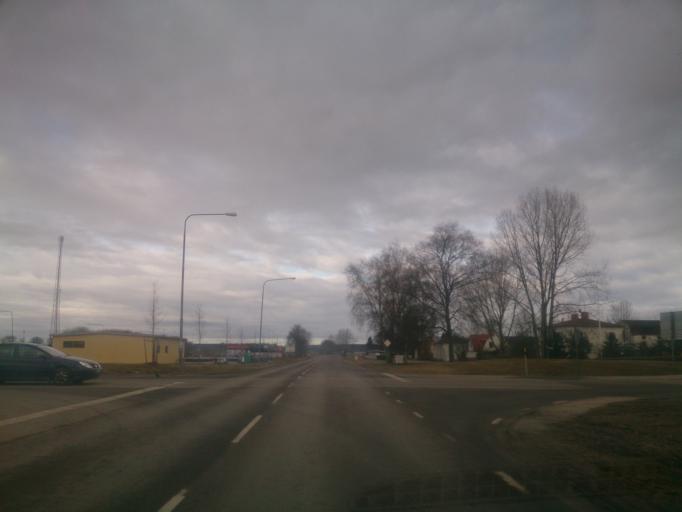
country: SE
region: OEstergoetland
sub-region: Motala Kommun
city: Borensberg
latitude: 58.4782
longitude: 15.2323
